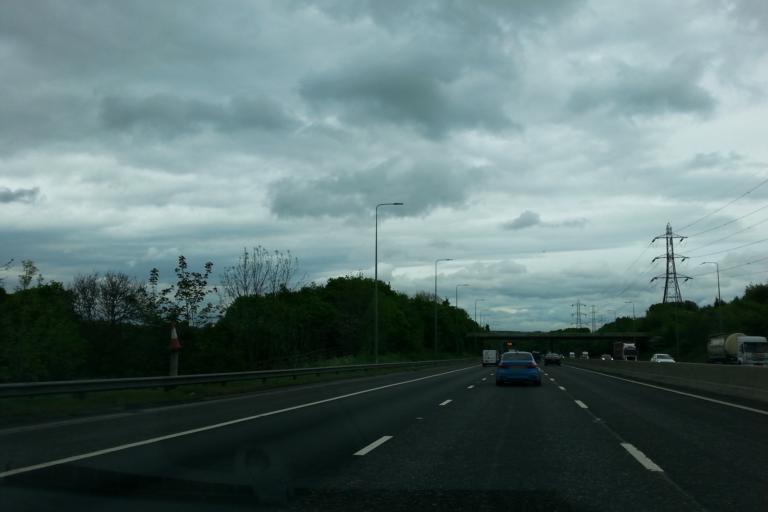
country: GB
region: England
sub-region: Calderdale
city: Brighouse
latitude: 53.6842
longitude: -1.7754
